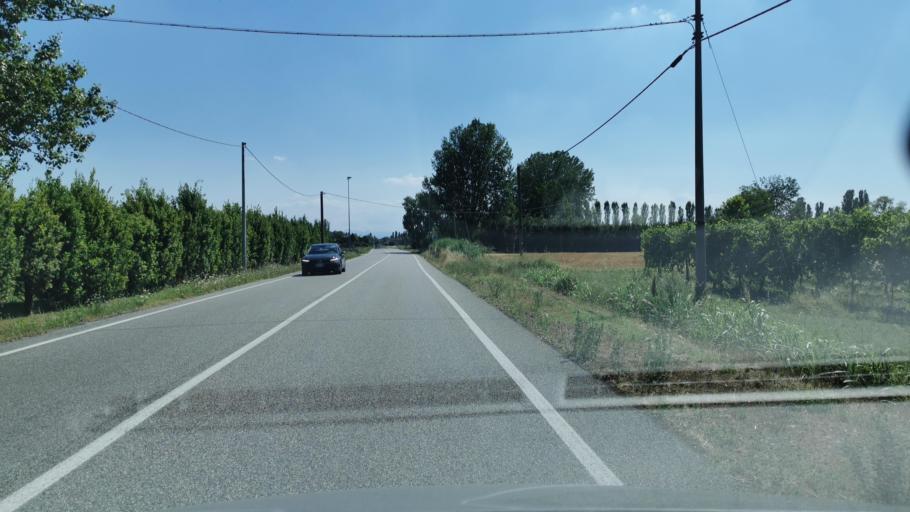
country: IT
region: Emilia-Romagna
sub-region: Provincia di Modena
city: Sam Marino
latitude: 44.7886
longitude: 10.9088
